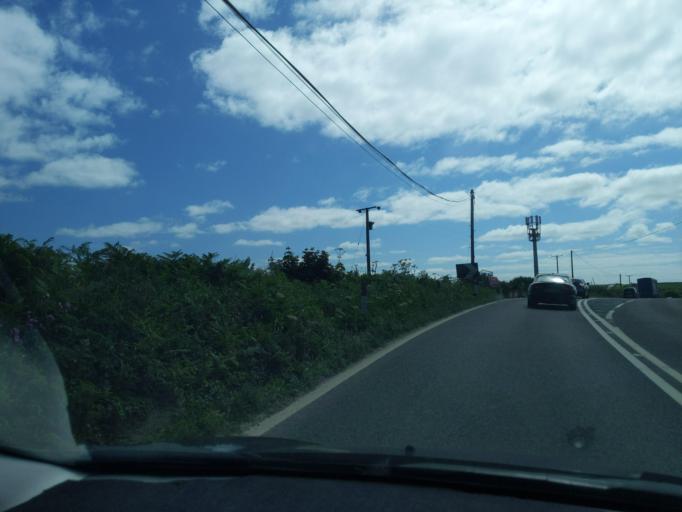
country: GB
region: England
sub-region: Cornwall
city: Truro
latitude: 50.3065
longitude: -5.0981
